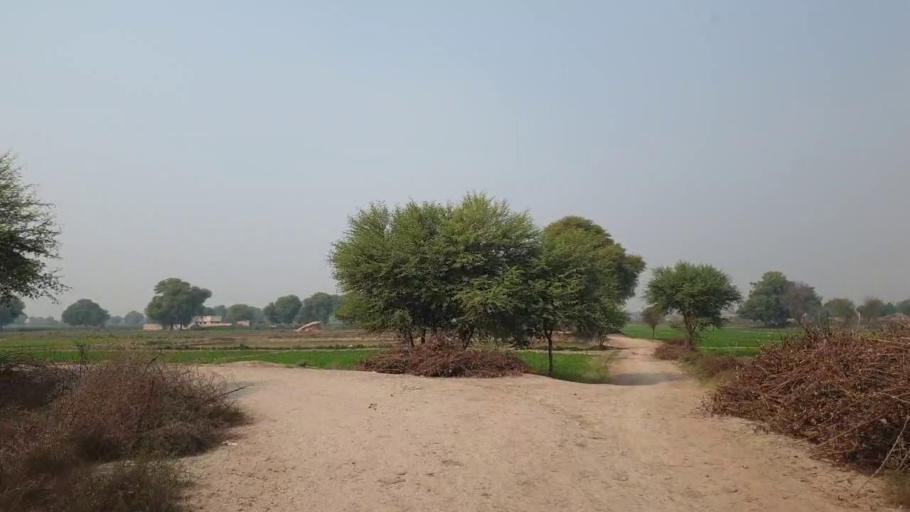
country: PK
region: Sindh
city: Bhan
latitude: 26.5315
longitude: 67.7121
